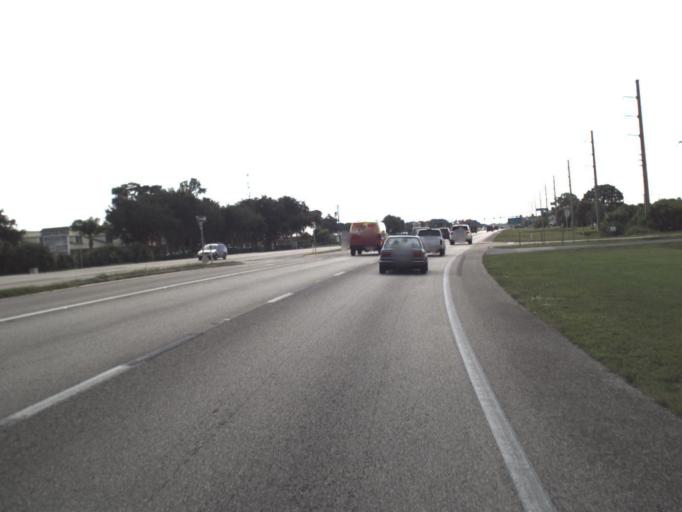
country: US
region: Florida
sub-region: Charlotte County
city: Port Charlotte
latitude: 27.0177
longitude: -82.1570
